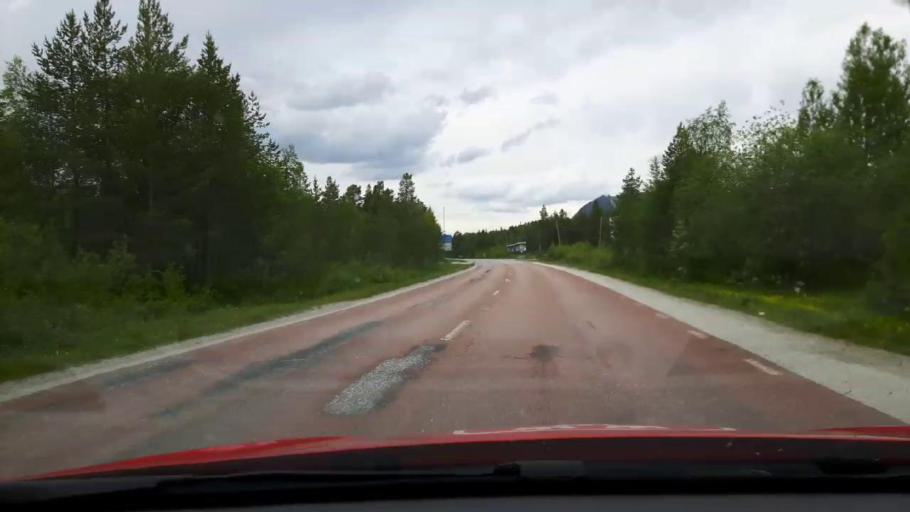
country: NO
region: Hedmark
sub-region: Engerdal
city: Engerdal
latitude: 62.5223
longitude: 12.5910
